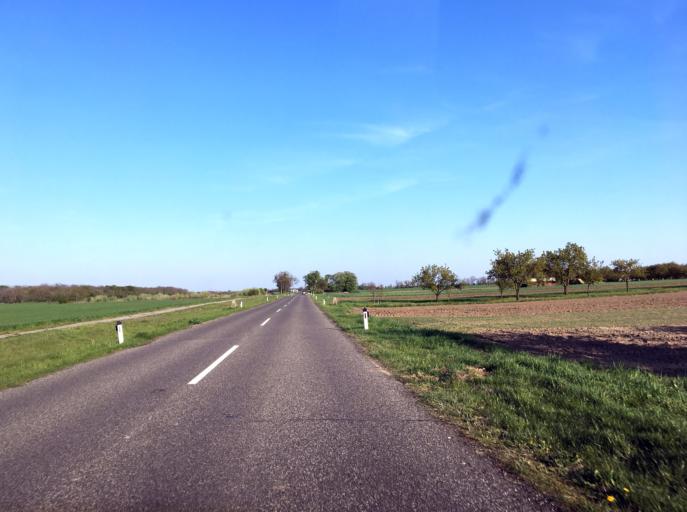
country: AT
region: Burgenland
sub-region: Politischer Bezirk Neusiedl am See
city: Kittsee
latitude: 48.0798
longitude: 17.0746
